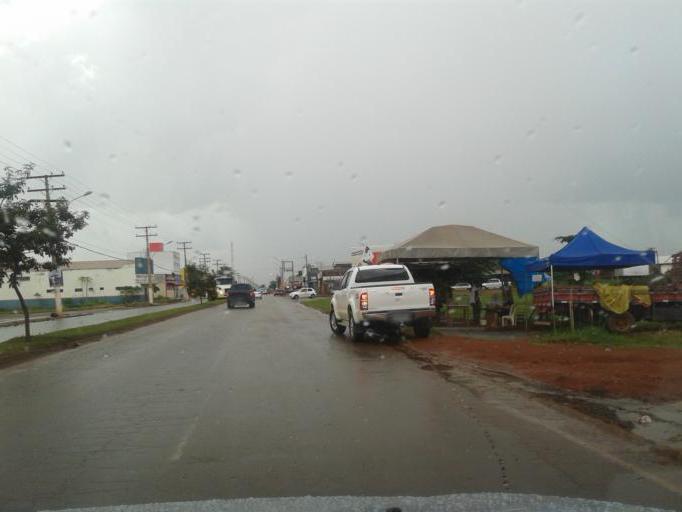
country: BR
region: Goias
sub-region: Itaberai
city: Itaberai
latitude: -16.0428
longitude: -49.7911
